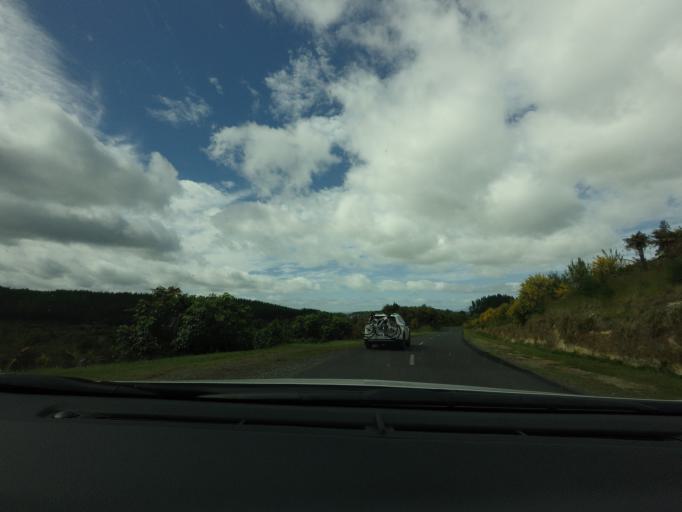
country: NZ
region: Bay of Plenty
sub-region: Rotorua District
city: Rotorua
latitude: -38.3479
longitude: 176.3701
